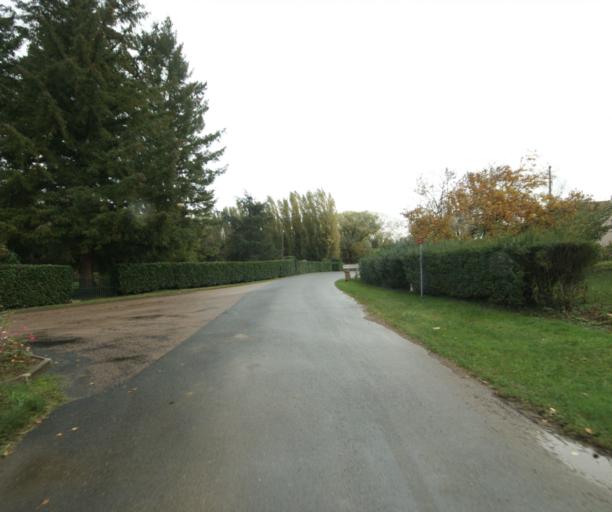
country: FR
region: Rhone-Alpes
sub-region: Departement de l'Ain
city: Pont-de-Vaux
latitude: 46.4730
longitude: 4.8829
